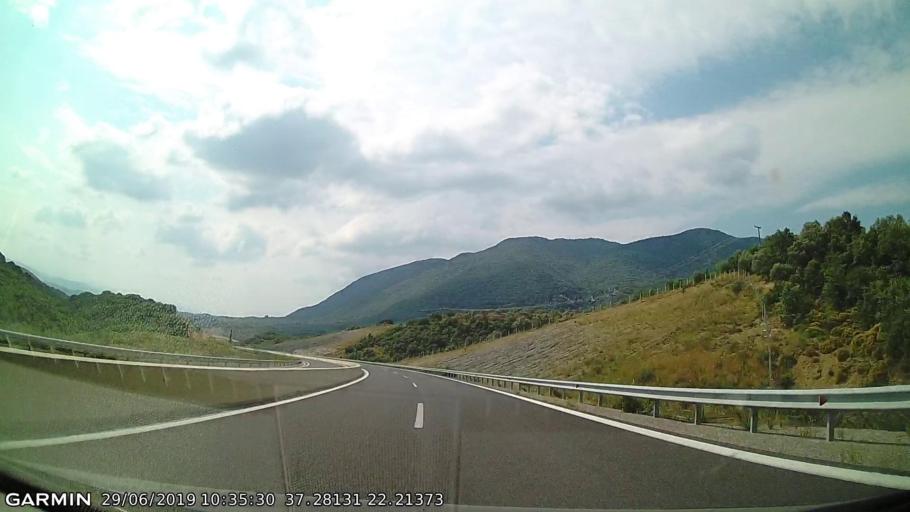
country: GR
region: Peloponnese
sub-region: Nomos Arkadias
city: Megalopoli
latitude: 37.2810
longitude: 22.2138
